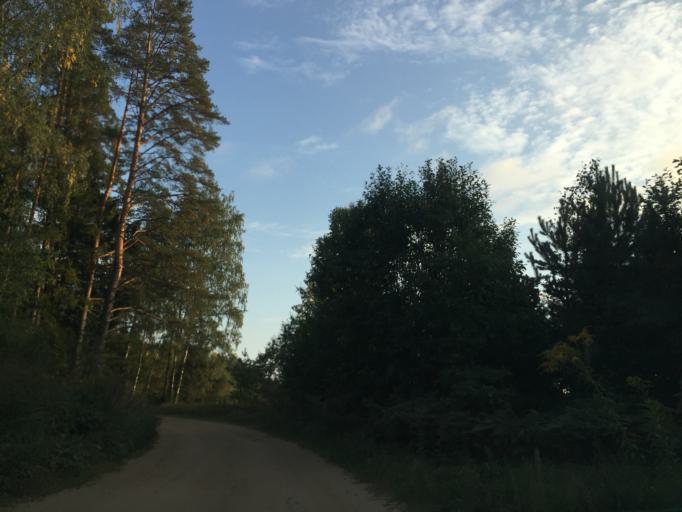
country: LV
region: Baldone
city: Baldone
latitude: 56.7628
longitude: 24.4090
